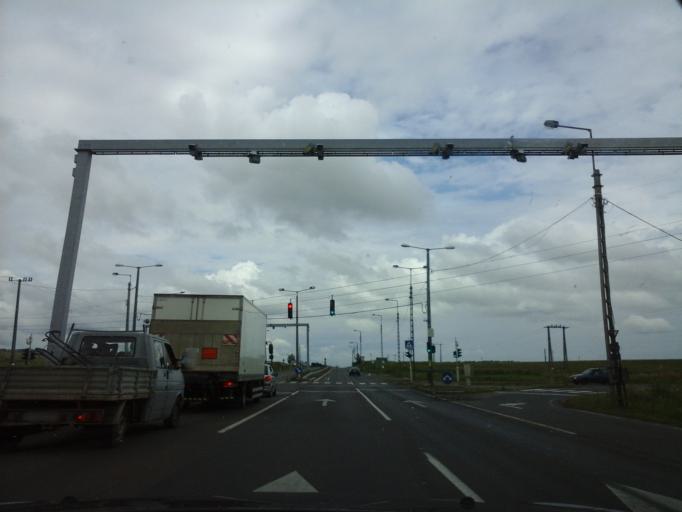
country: HU
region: Borsod-Abauj-Zemplen
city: Sajobabony
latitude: 48.1832
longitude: 20.7575
